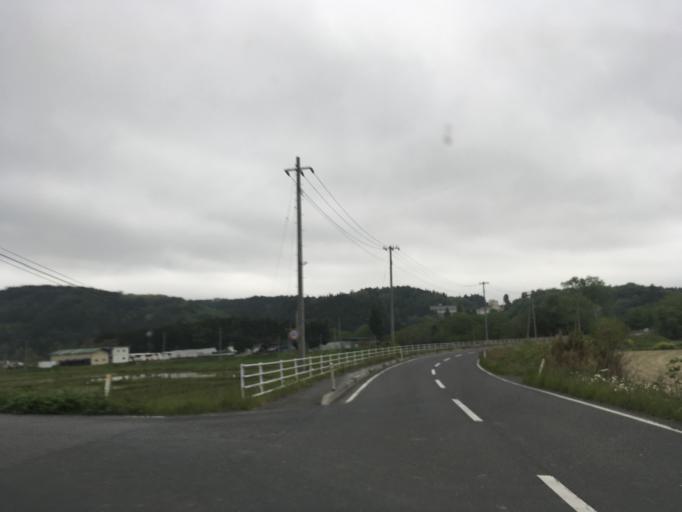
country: JP
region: Miyagi
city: Wakuya
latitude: 38.7181
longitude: 141.2960
